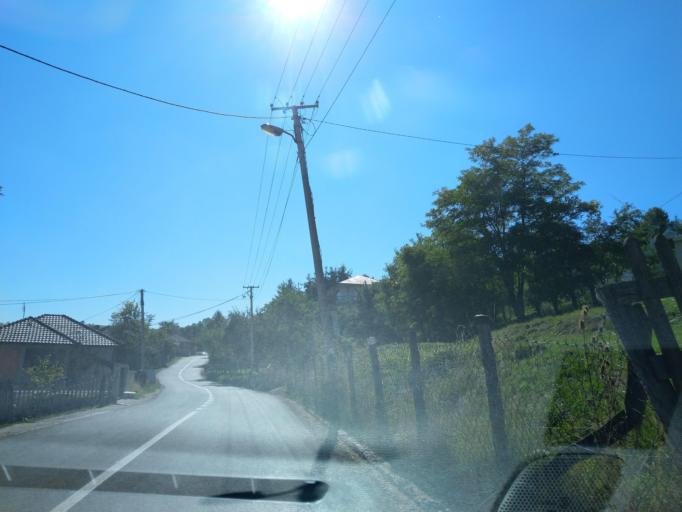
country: RS
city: Sokolovica
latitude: 43.2521
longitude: 20.2281
